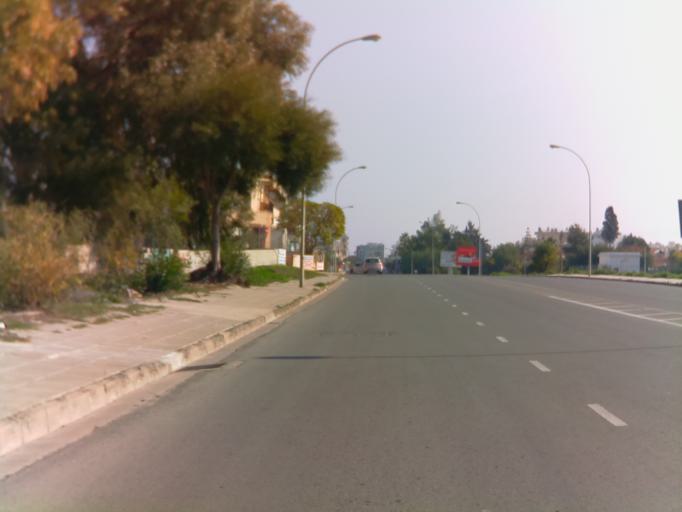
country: CY
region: Larnaka
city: Larnaca
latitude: 34.9112
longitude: 33.6153
